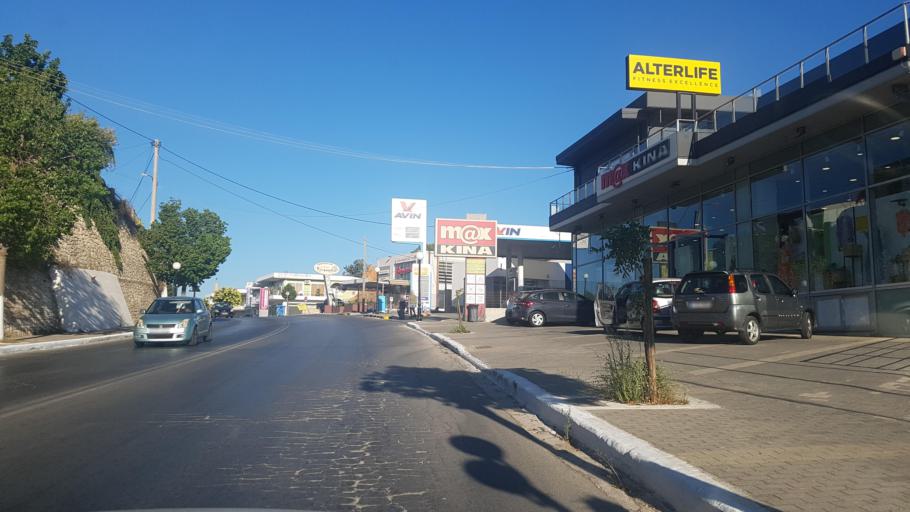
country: GR
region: Crete
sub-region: Nomos Chanias
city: Daratsos
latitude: 35.5069
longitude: 23.9833
